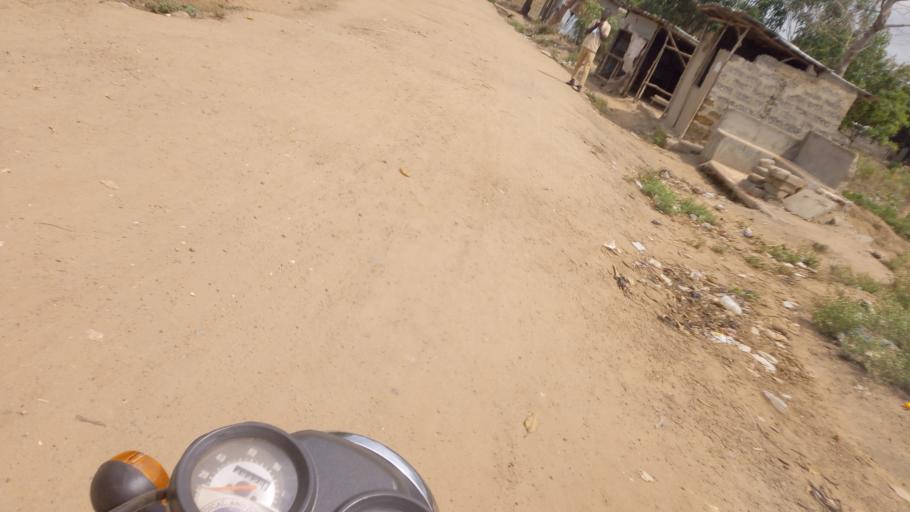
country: SL
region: Western Area
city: Waterloo
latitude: 8.3102
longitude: -13.0657
